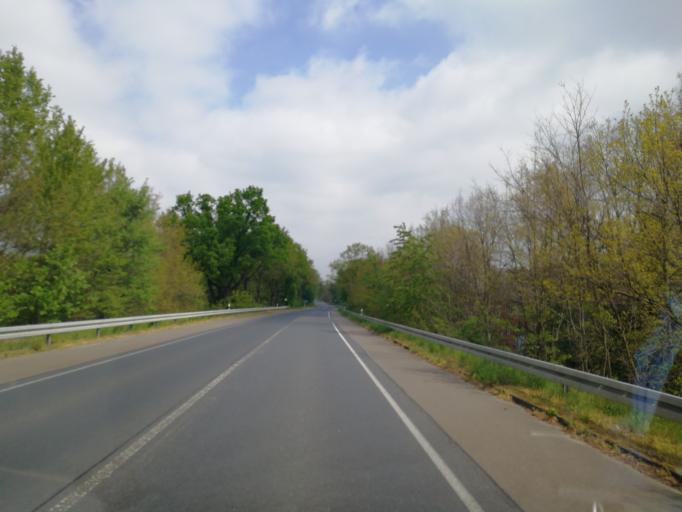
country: DE
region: Brandenburg
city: Herzberg
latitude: 51.6421
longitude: 13.1767
